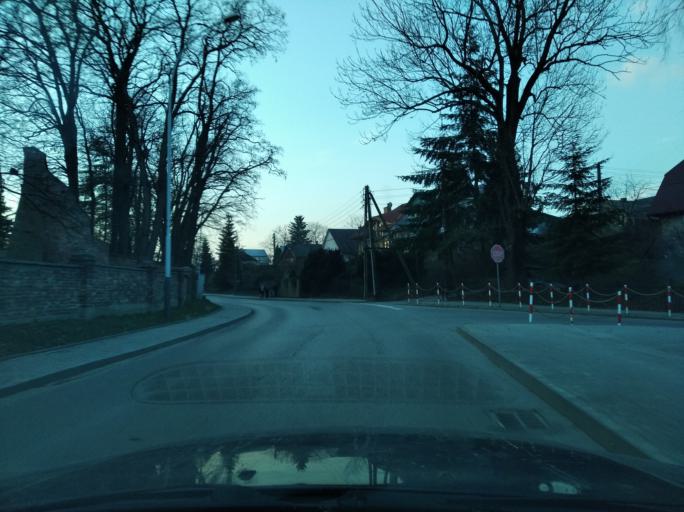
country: PL
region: Subcarpathian Voivodeship
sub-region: Powiat przeworski
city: Przeworsk
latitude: 50.0553
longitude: 22.4998
